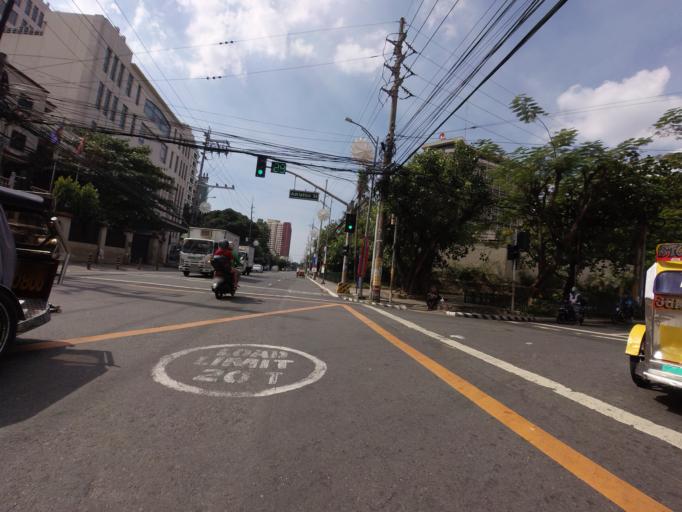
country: PH
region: Metro Manila
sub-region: City of Manila
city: Port Area
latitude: 14.5610
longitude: 120.9923
